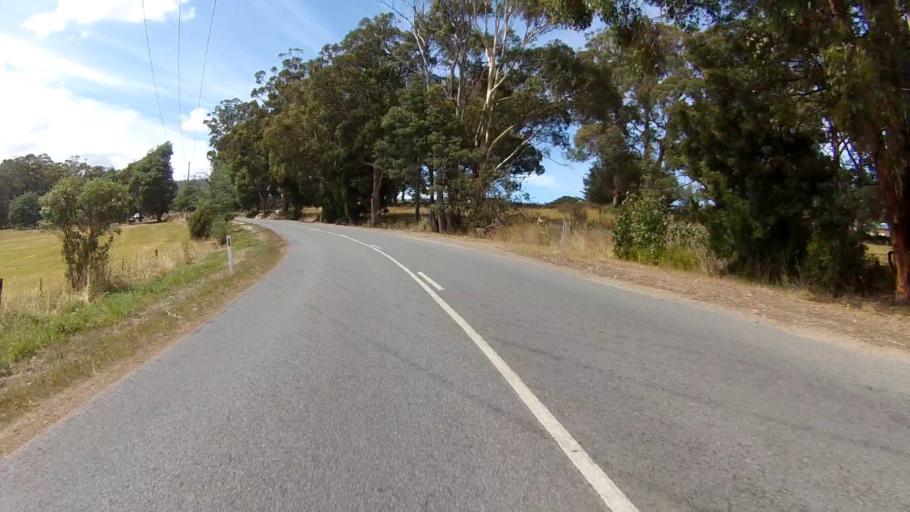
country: AU
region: Tasmania
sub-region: Huon Valley
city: Cygnet
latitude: -43.2135
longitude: 147.1176
